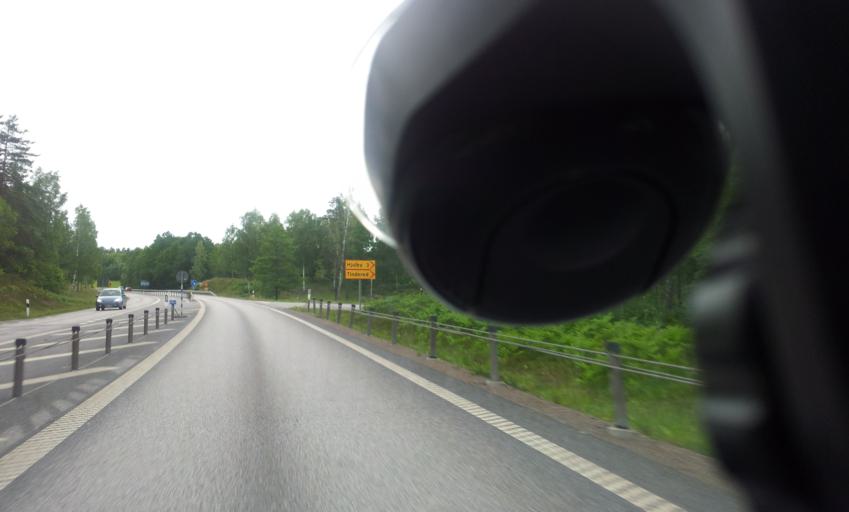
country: SE
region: Kalmar
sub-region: Vasterviks Kommun
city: Forserum
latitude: 57.9743
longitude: 16.4838
